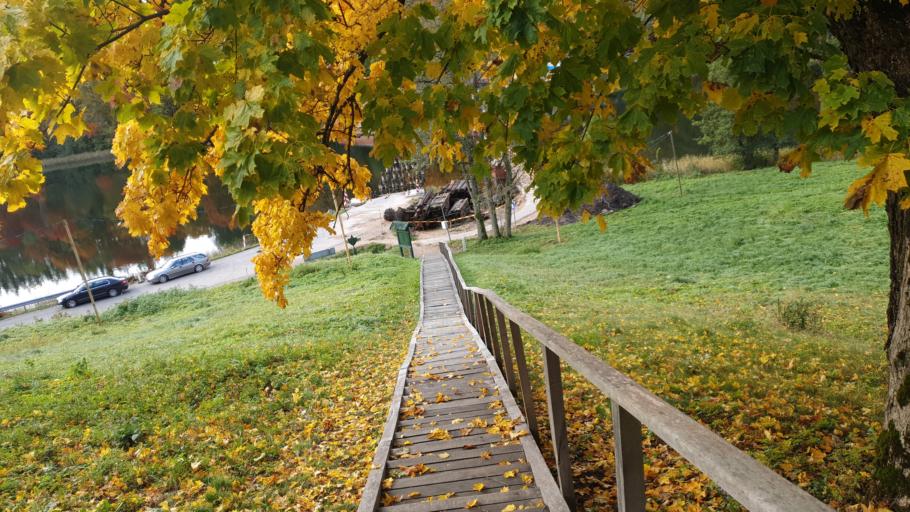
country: LT
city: Moletai
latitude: 55.0579
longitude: 25.4448
